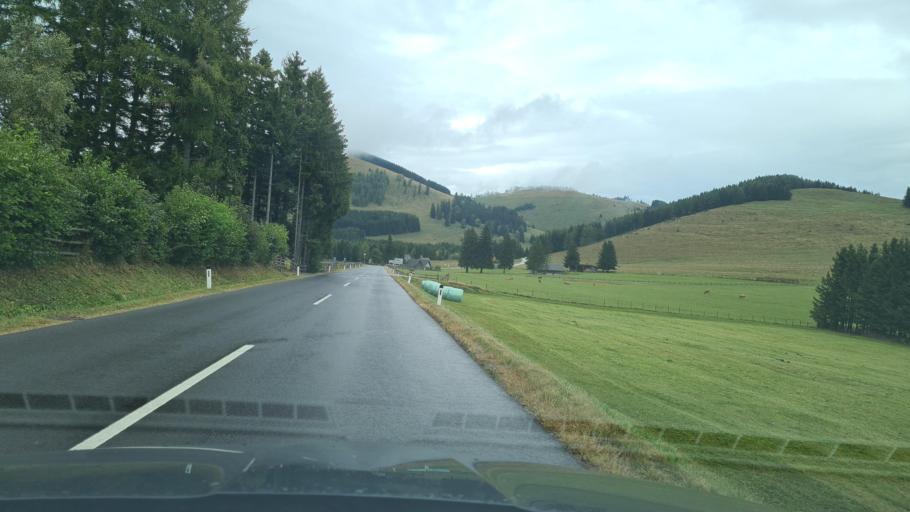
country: AT
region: Styria
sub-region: Politischer Bezirk Weiz
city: Passail
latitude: 47.3394
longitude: 15.4770
